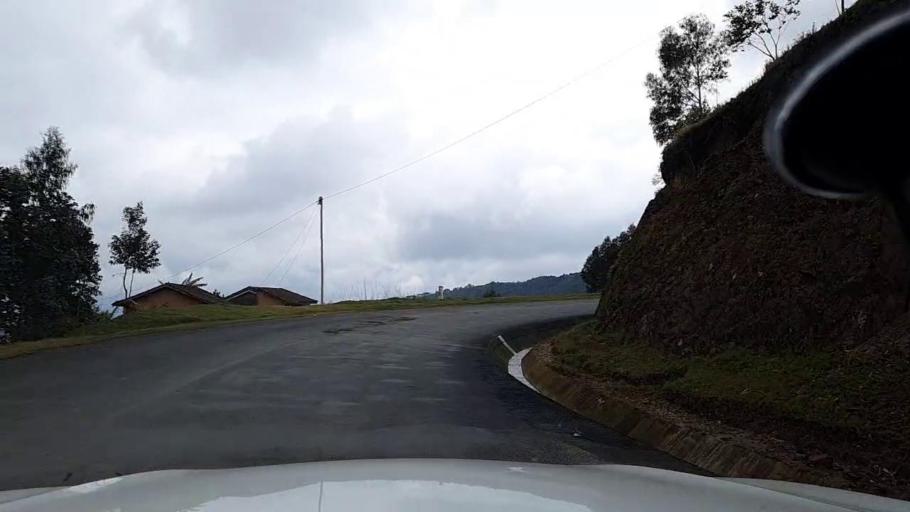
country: RW
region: Western Province
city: Kibuye
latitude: -2.0586
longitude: 29.5153
